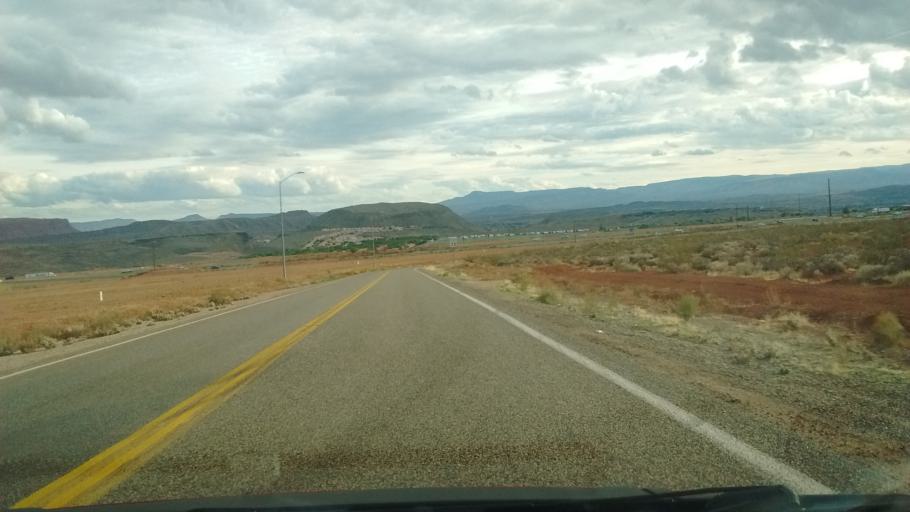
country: US
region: Utah
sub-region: Washington County
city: Washington
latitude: 37.1495
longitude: -113.4923
